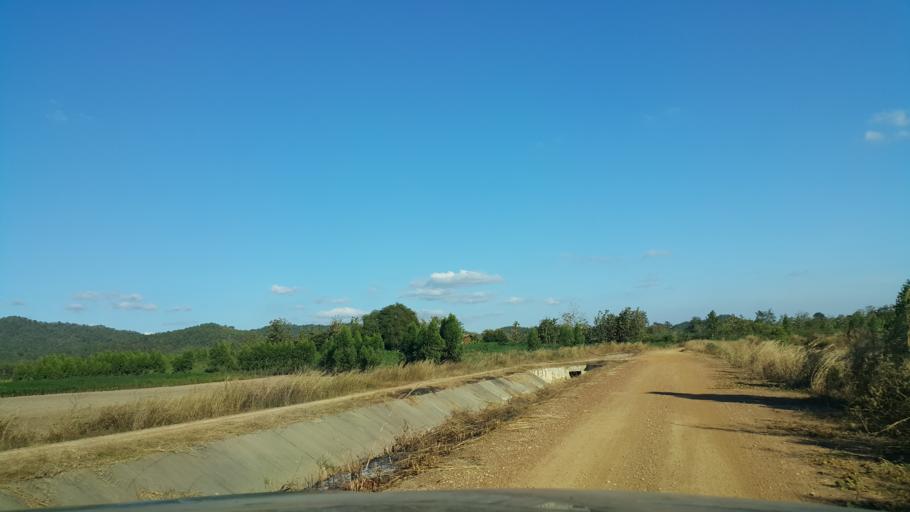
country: TH
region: Sukhothai
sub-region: Amphoe Si Satchanalai
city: Si Satchanalai
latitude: 17.4739
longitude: 99.6569
